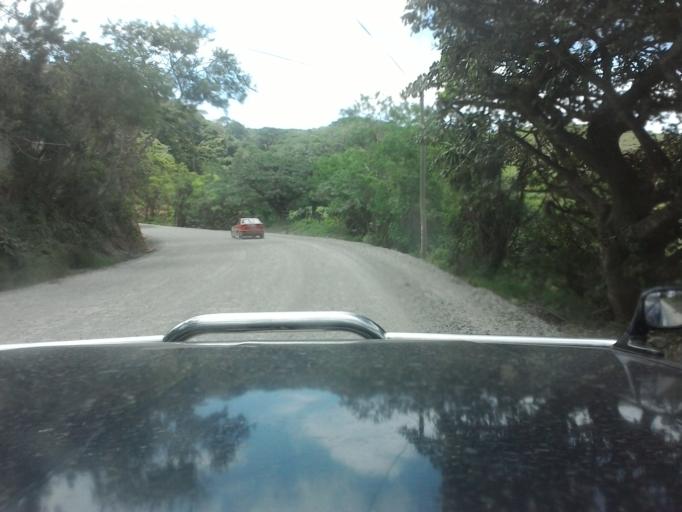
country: CR
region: Guanacaste
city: Juntas
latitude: 10.2618
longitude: -84.8415
